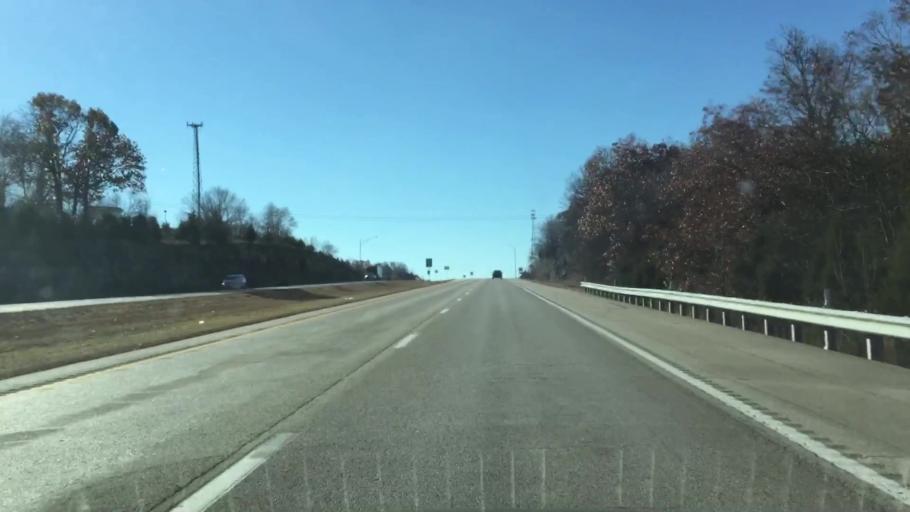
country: US
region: Missouri
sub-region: Cole County
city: Wardsville
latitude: 38.4871
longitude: -92.2714
